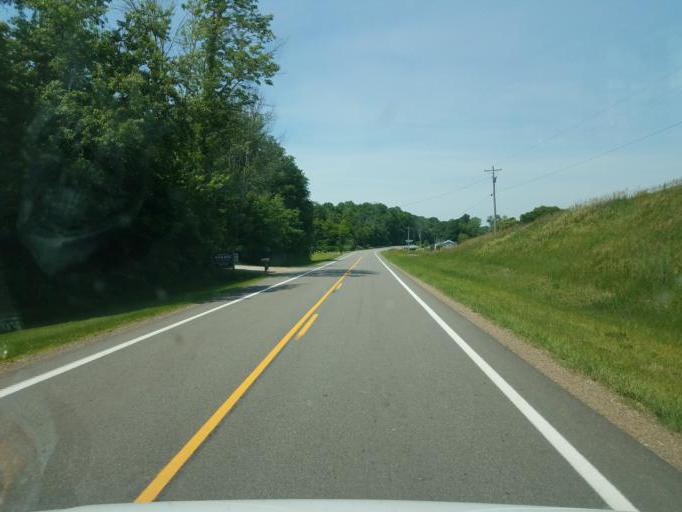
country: US
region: Ohio
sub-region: Ashland County
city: Loudonville
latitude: 40.6537
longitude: -82.3280
